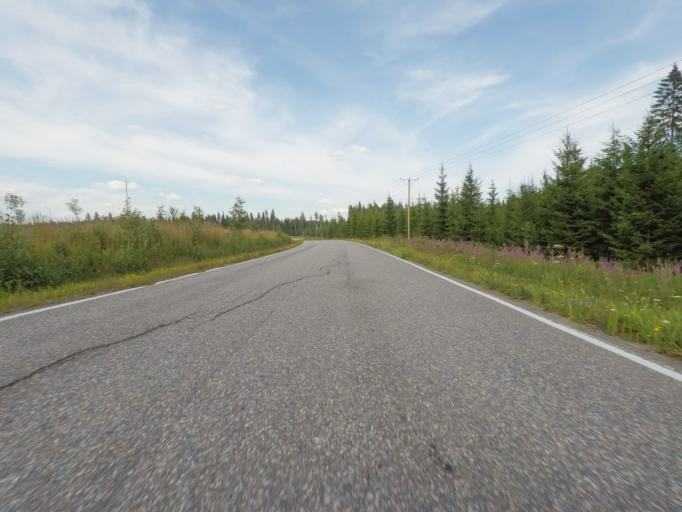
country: FI
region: Southern Savonia
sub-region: Savonlinna
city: Sulkava
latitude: 61.7471
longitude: 28.2002
